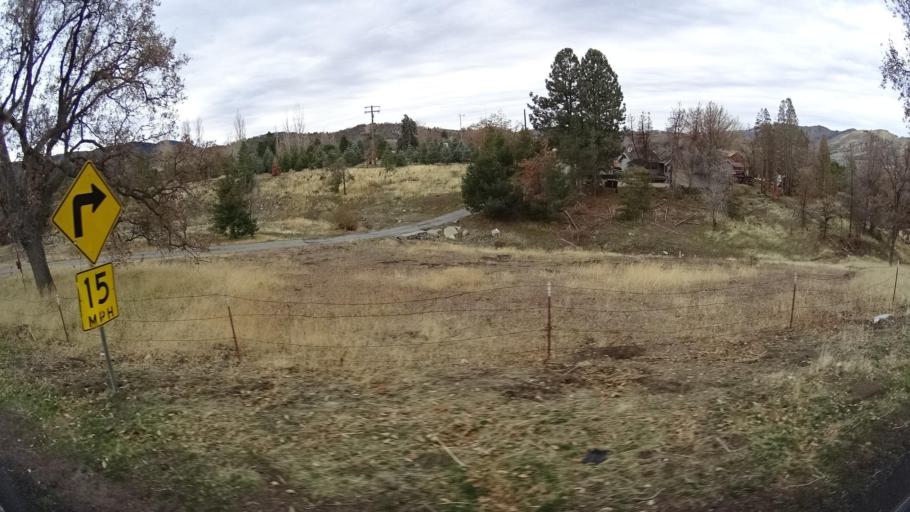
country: US
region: California
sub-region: Kern County
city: Golden Hills
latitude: 35.1042
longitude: -118.5261
